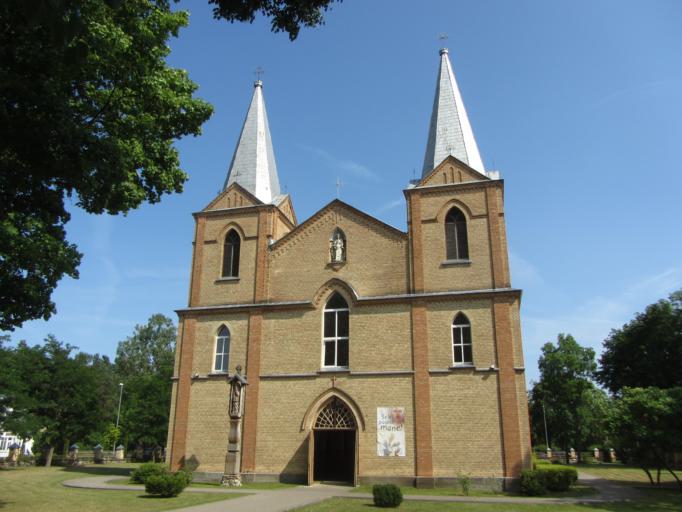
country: LT
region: Alytaus apskritis
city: Druskininkai
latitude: 53.9976
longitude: 24.0190
